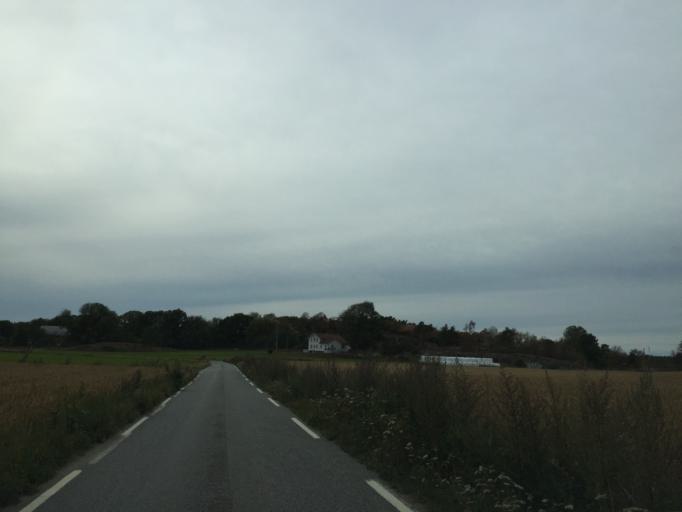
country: NO
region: Ostfold
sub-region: Hvaler
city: Skjaerhalden
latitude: 59.0393
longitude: 11.0454
